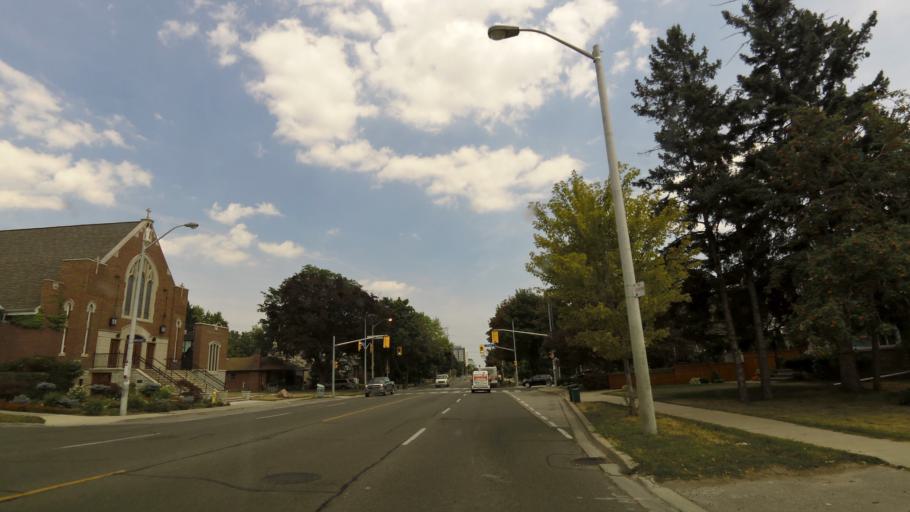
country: CA
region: Ontario
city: Etobicoke
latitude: 43.6395
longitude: -79.5453
